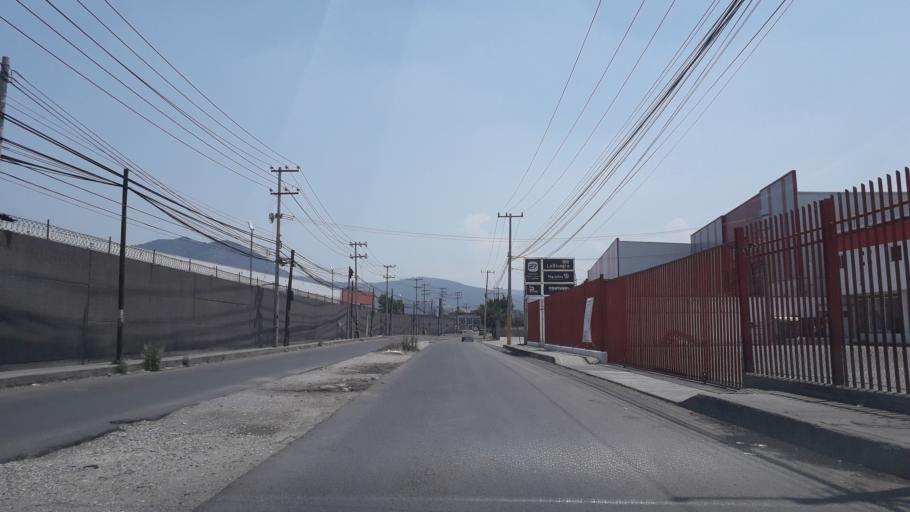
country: MX
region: Mexico
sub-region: Tultitlan
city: Colonia Lazaro Cardenas (Los Hornos)
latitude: 19.6306
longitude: -99.1529
